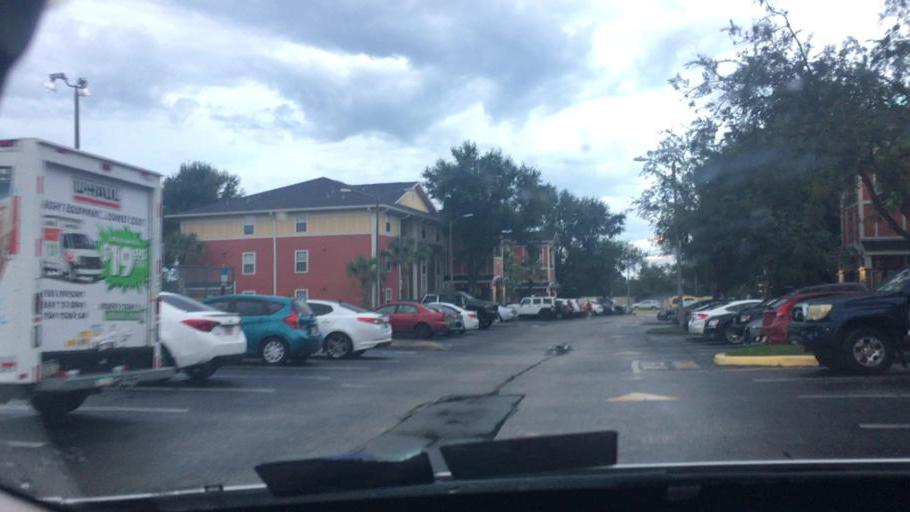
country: US
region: Florida
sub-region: Orange County
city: Alafaya
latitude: 28.6104
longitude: -81.2123
